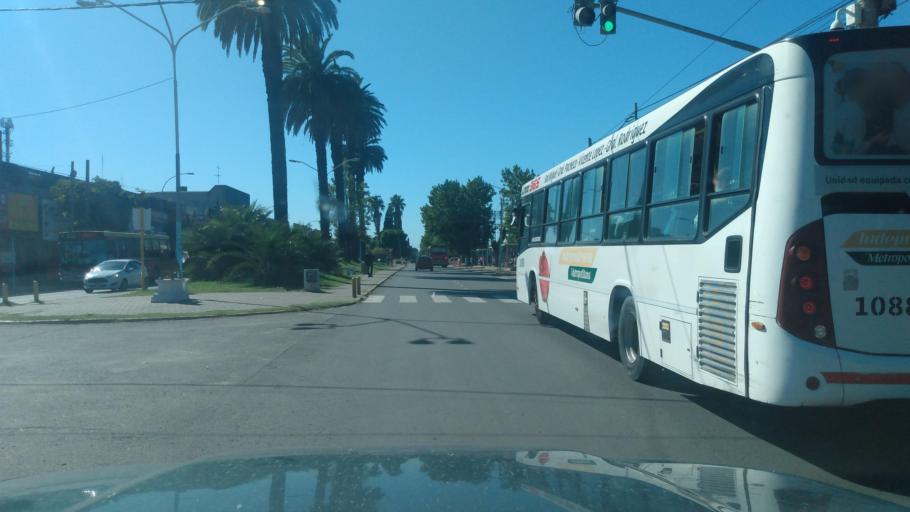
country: AR
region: Buenos Aires
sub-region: Partido de General Rodriguez
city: General Rodriguez
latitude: -34.6086
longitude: -58.9530
